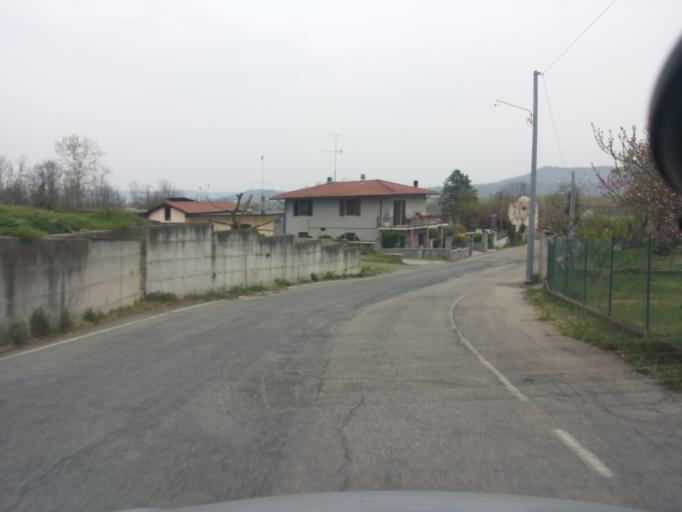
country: IT
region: Piedmont
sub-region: Provincia di Torino
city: Caravino
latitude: 45.4014
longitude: 7.9640
